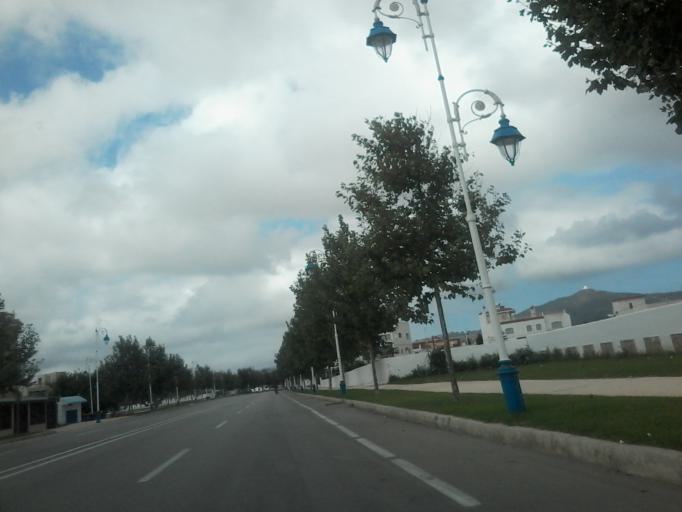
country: MA
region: Tanger-Tetouan
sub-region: Tetouan
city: Martil
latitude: 35.6400
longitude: -5.2915
